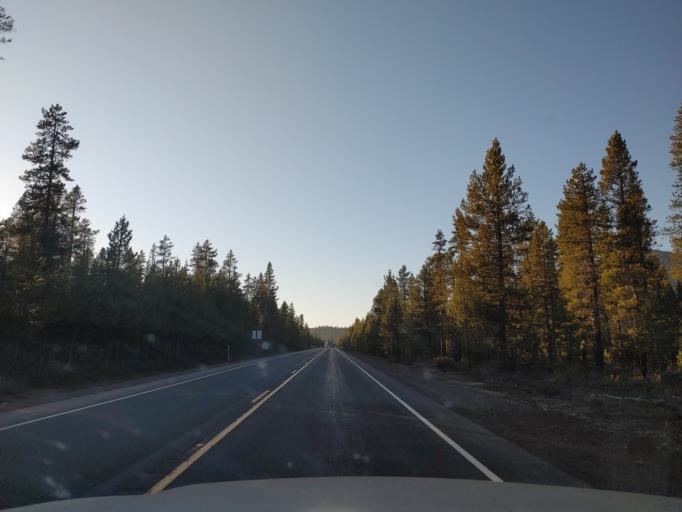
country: US
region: Oregon
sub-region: Deschutes County
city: La Pine
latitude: 43.4312
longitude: -121.8540
